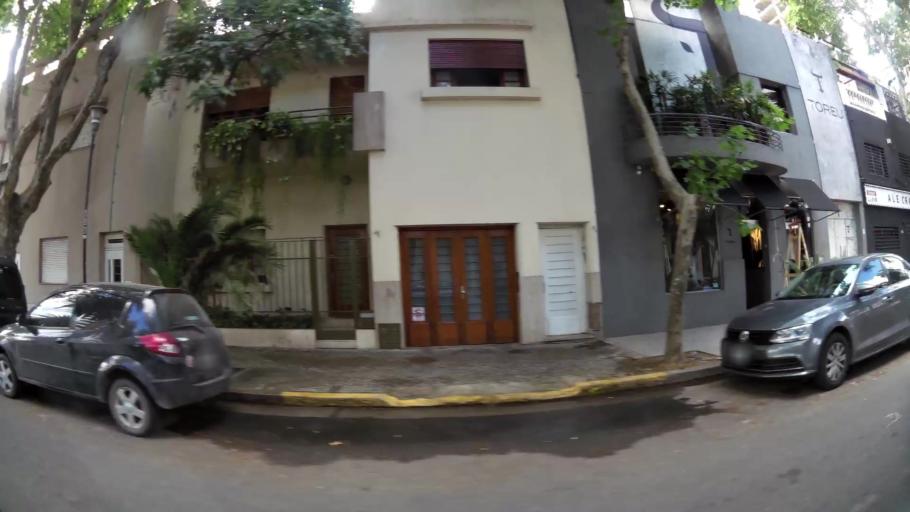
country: AR
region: Santa Fe
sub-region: Departamento de Rosario
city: Rosario
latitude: -32.9330
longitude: -60.6504
